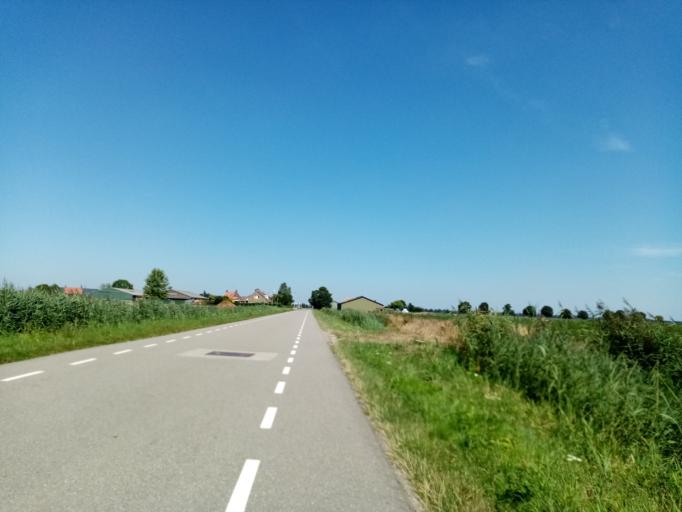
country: NL
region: North Brabant
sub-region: Gemeente Breda
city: Breda
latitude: 51.6482
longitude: 4.6971
